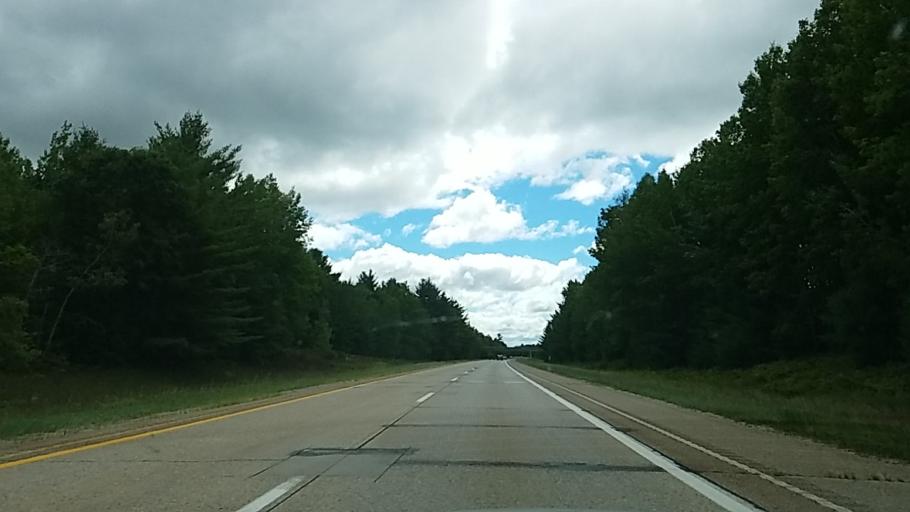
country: US
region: Michigan
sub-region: Ogemaw County
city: West Branch
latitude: 44.1800
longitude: -84.1763
